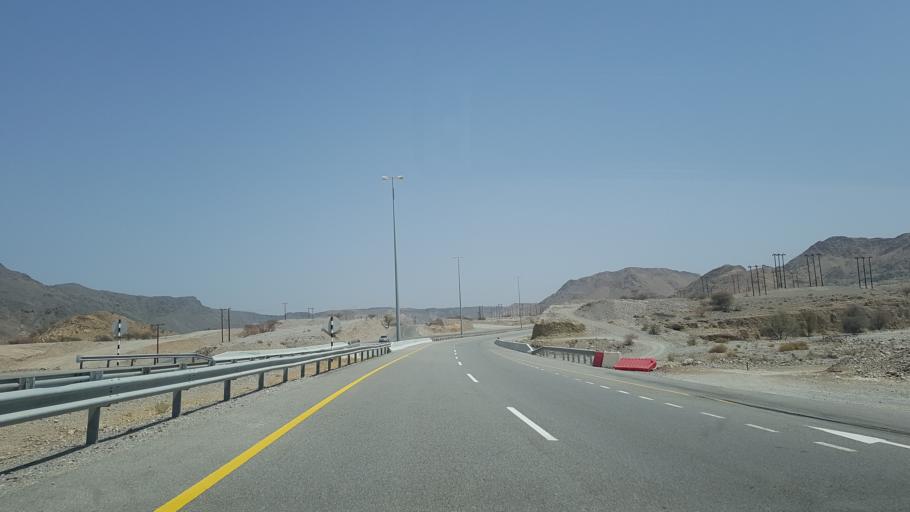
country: OM
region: Muhafazat Masqat
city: Muscat
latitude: 23.2460
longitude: 58.7909
